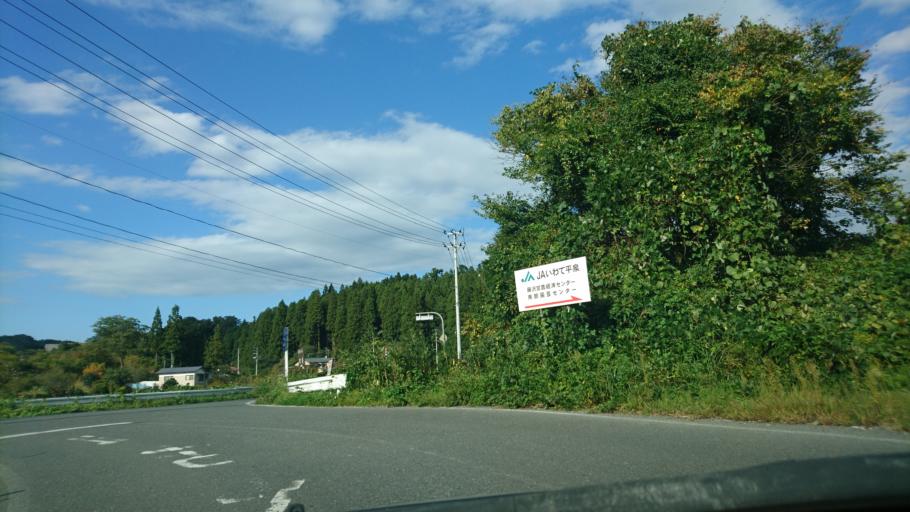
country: JP
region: Iwate
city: Ichinoseki
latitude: 38.8996
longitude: 141.3247
